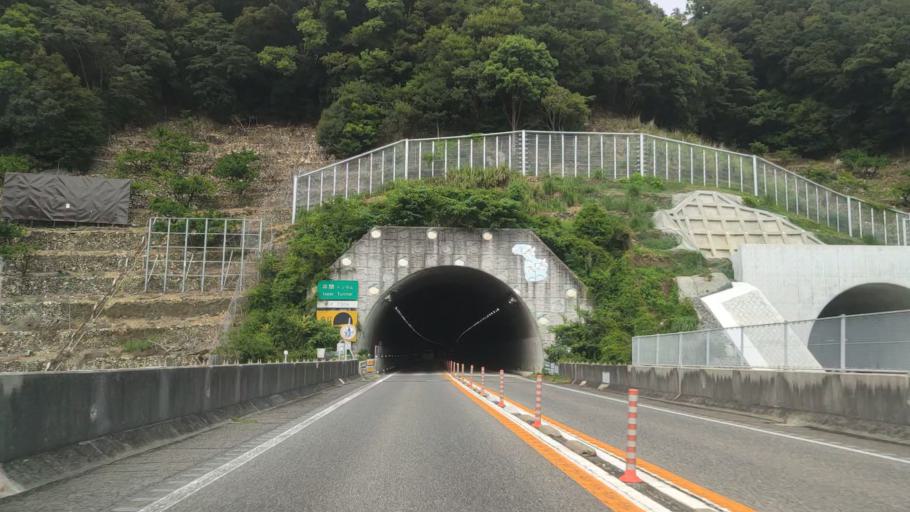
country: JP
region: Wakayama
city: Gobo
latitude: 33.9989
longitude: 135.1960
